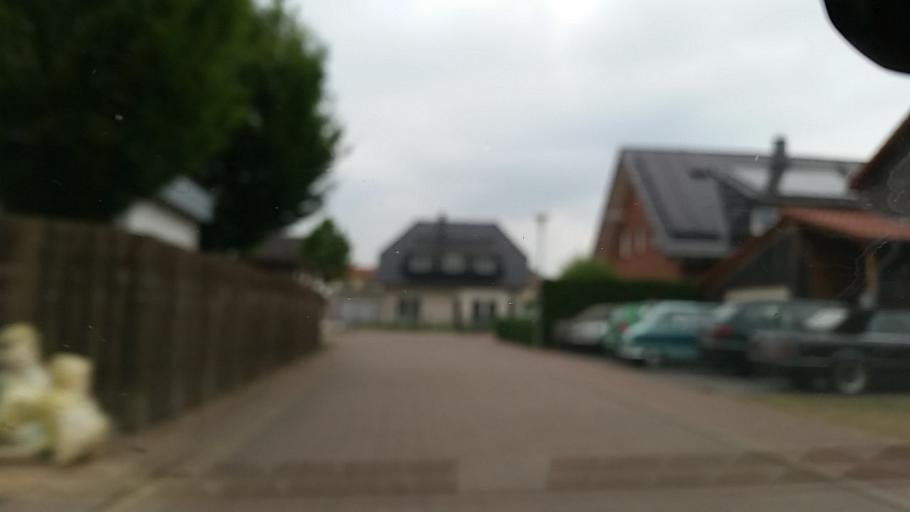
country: DE
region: Lower Saxony
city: Wolfsburg
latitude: 52.3929
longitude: 10.7238
